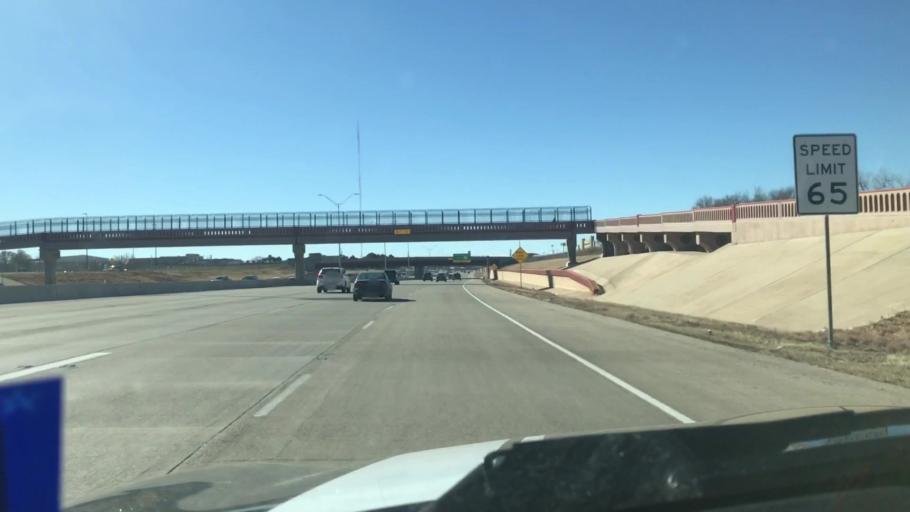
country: US
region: Texas
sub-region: Lubbock County
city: Lubbock
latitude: 33.5896
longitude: -101.8813
